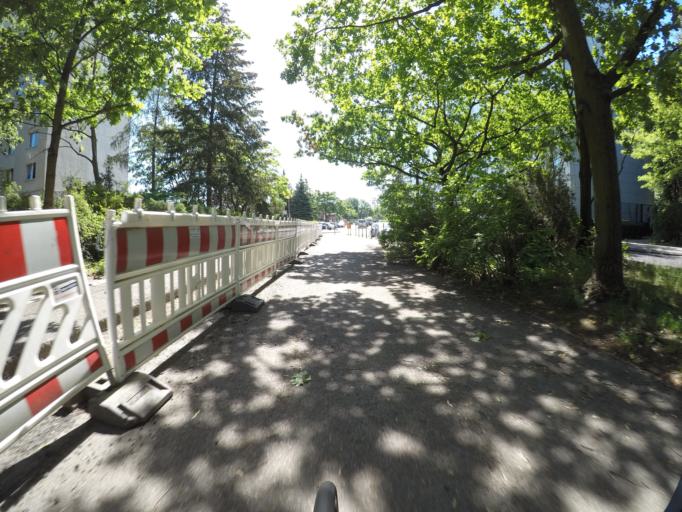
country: DE
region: Berlin
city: Weissensee
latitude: 52.5402
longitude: 13.4507
